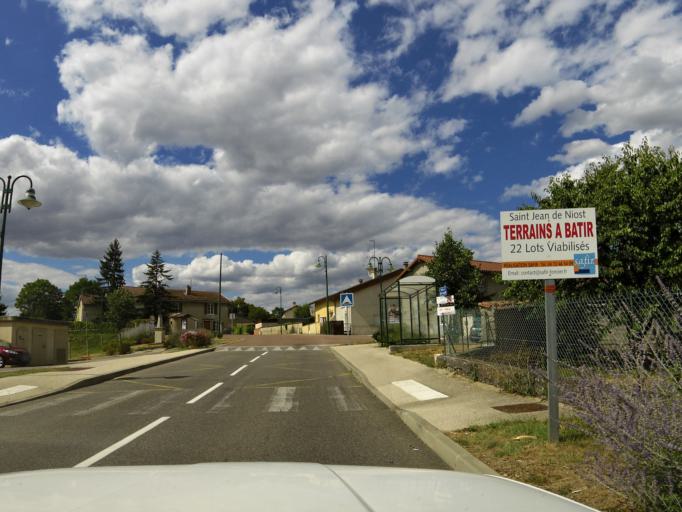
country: FR
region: Rhone-Alpes
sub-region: Departement de l'Ain
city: Saint-Jean-de-Niost
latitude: 45.8337
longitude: 5.2213
